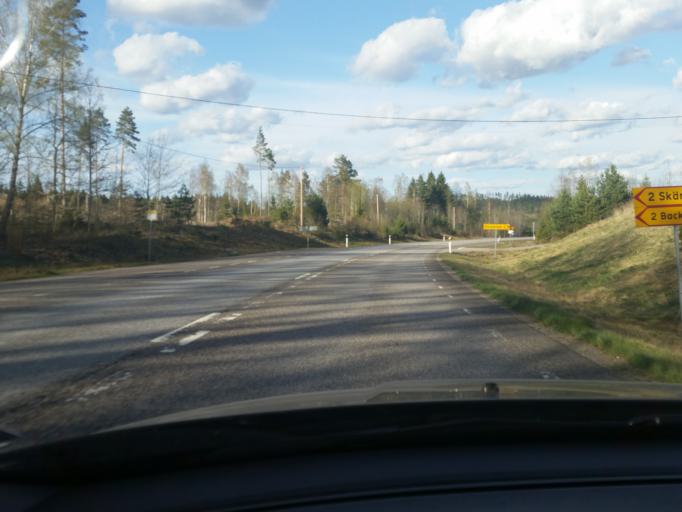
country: SE
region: Kalmar
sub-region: Hultsfreds Kommun
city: Virserum
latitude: 57.3639
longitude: 15.6496
